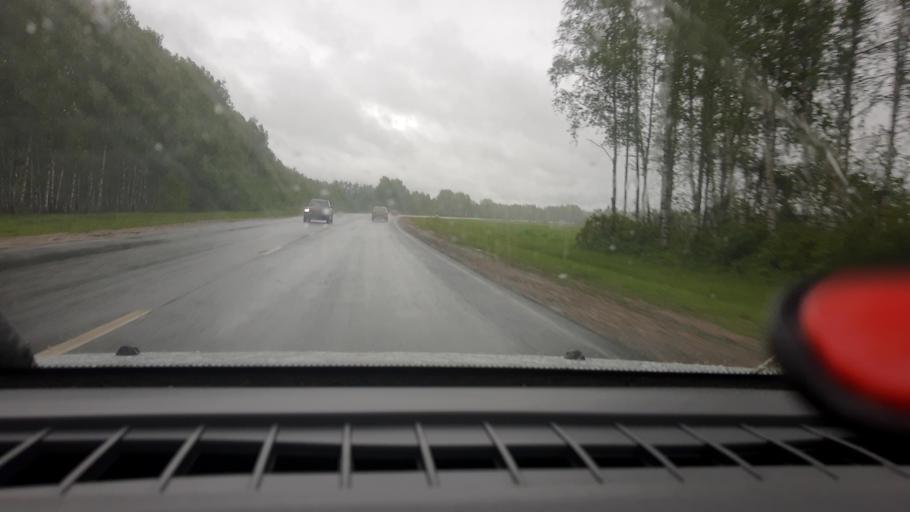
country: RU
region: Nizjnij Novgorod
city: Linda
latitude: 56.5753
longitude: 44.0229
